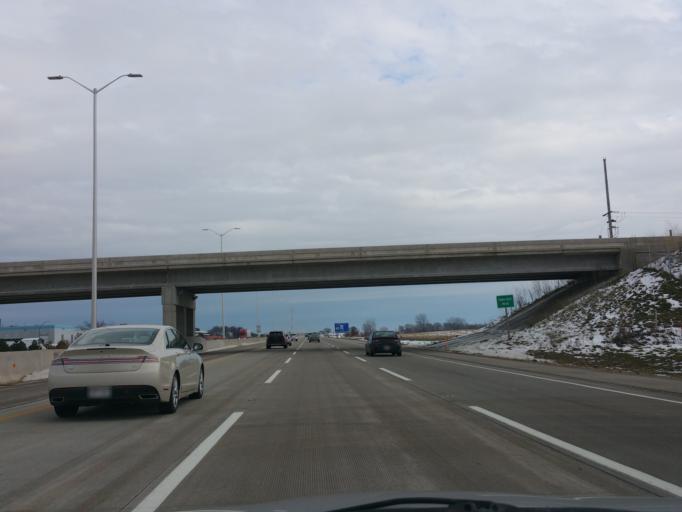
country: US
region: Illinois
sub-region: Boone County
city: Belvidere
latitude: 42.2331
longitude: -88.8818
